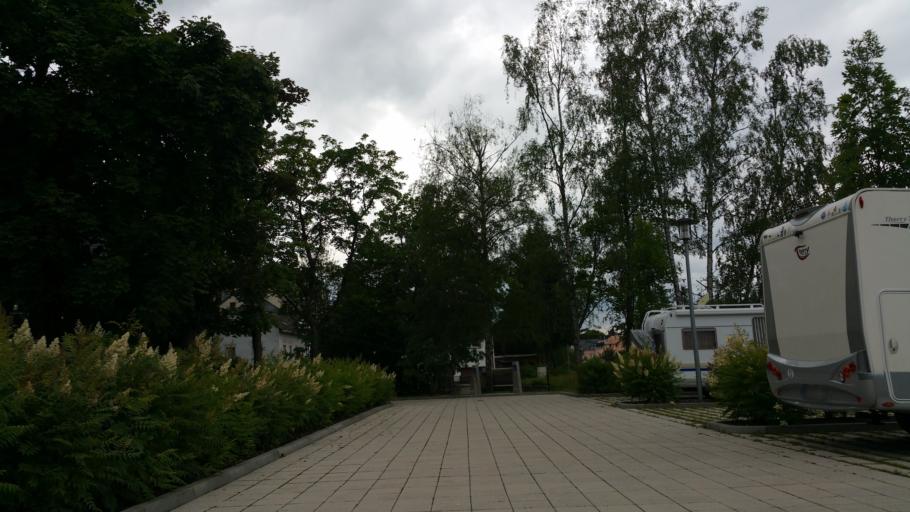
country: DE
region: Bavaria
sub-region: Upper Franconia
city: Oberkotzau
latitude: 50.2635
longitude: 11.9383
